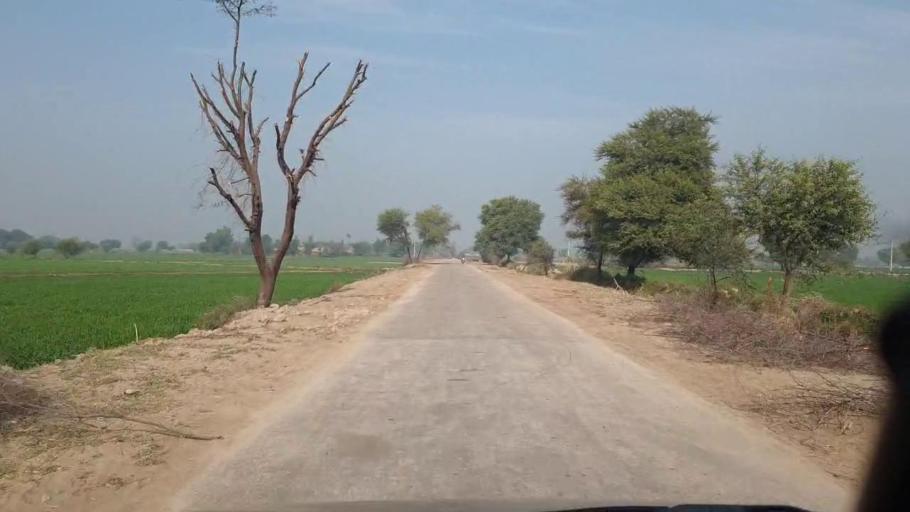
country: PK
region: Sindh
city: Shahdadpur
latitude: 26.0107
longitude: 68.5470
